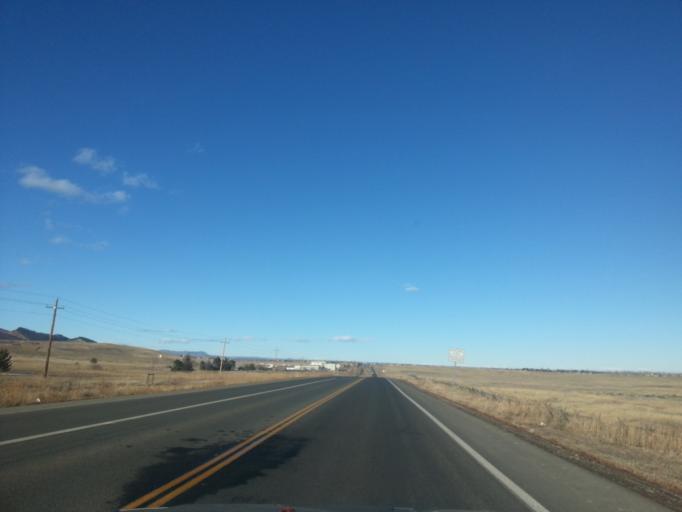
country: US
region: Colorado
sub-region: Larimer County
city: Fort Collins
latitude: 40.4946
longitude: -105.1155
